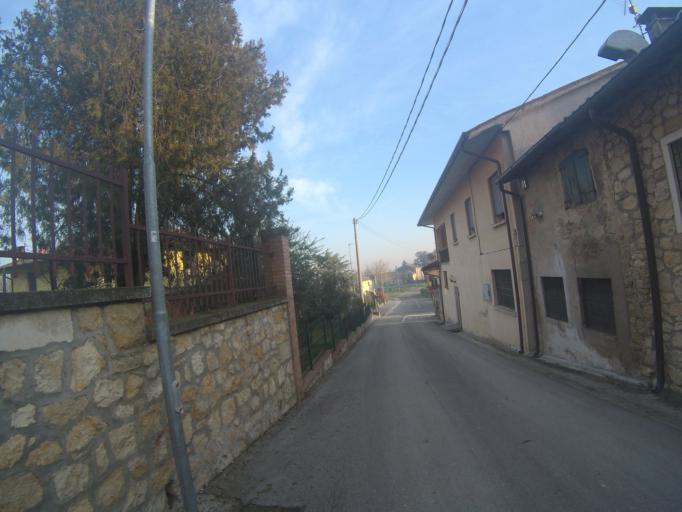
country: IT
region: Veneto
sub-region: Provincia di Vicenza
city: Ponte di Castegnero
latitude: 45.4433
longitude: 11.5861
